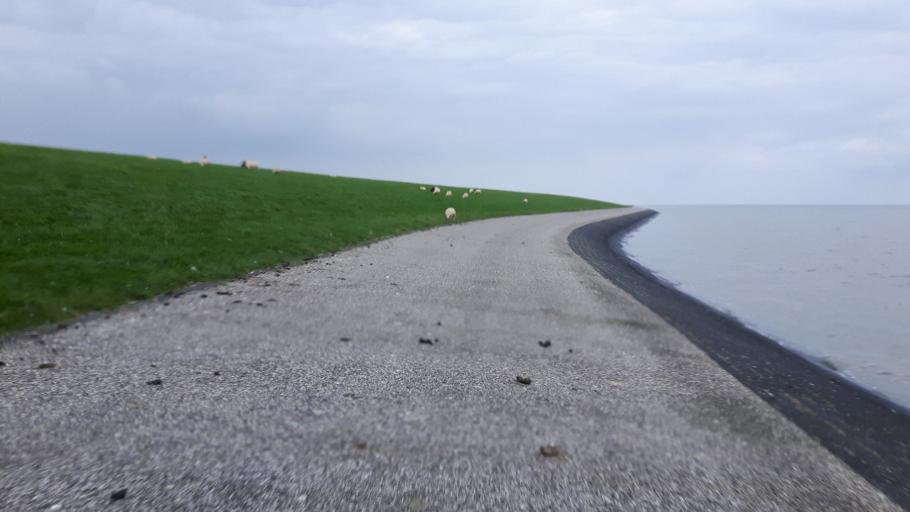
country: NL
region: Friesland
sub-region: Gemeente Ameland
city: Nes
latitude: 53.4442
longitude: 5.8426
